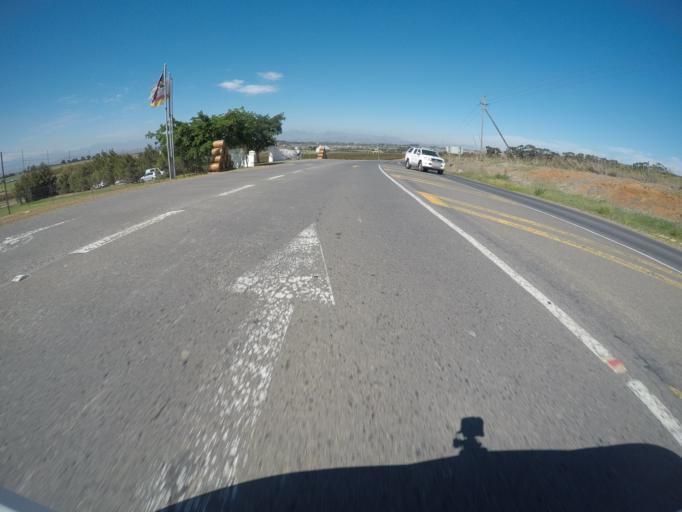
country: ZA
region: Western Cape
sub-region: City of Cape Town
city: Kraaifontein
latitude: -33.8024
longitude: 18.6191
